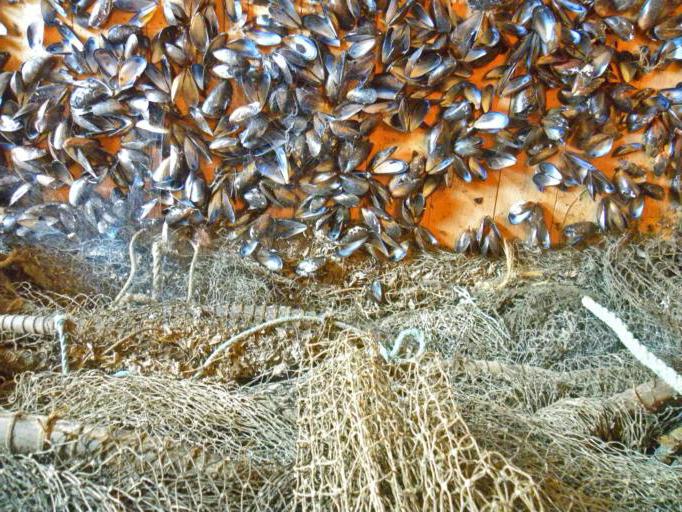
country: DK
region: Central Jutland
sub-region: Struer Kommune
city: Struer
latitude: 56.6531
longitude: 8.6369
